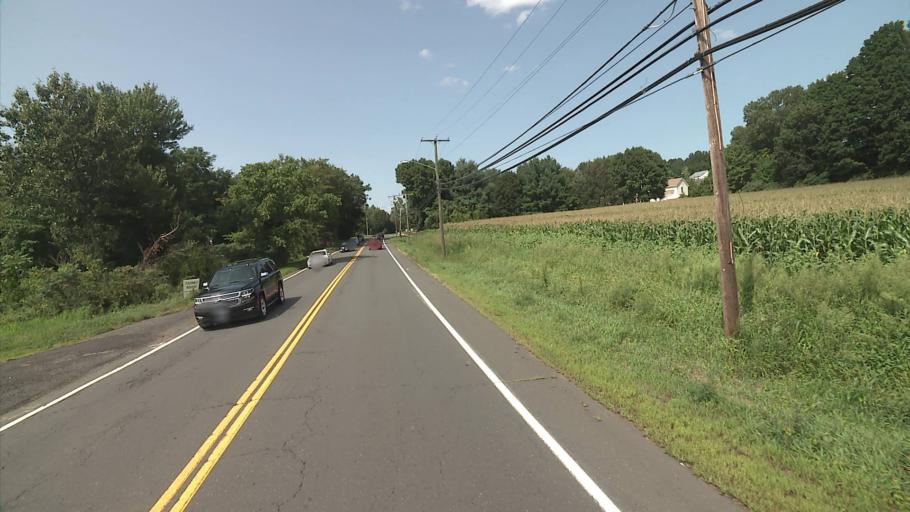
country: US
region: Connecticut
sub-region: Hartford County
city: South Windsor
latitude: 41.8325
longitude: -72.5558
